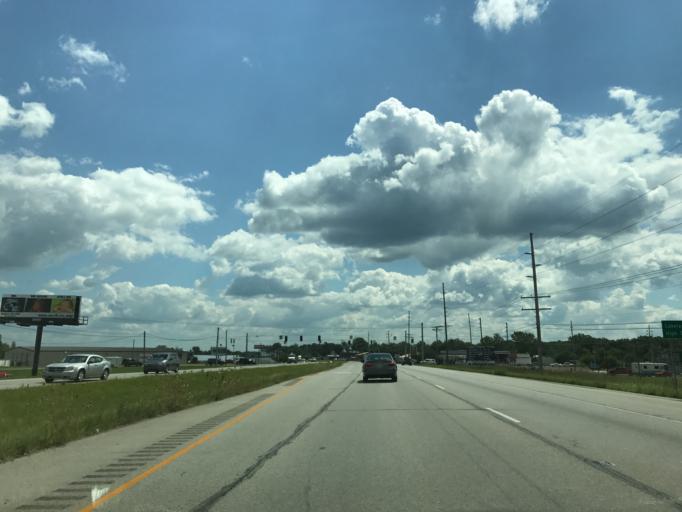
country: US
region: Indiana
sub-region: Kosciusko County
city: Winona Lake
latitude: 41.2272
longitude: -85.7960
